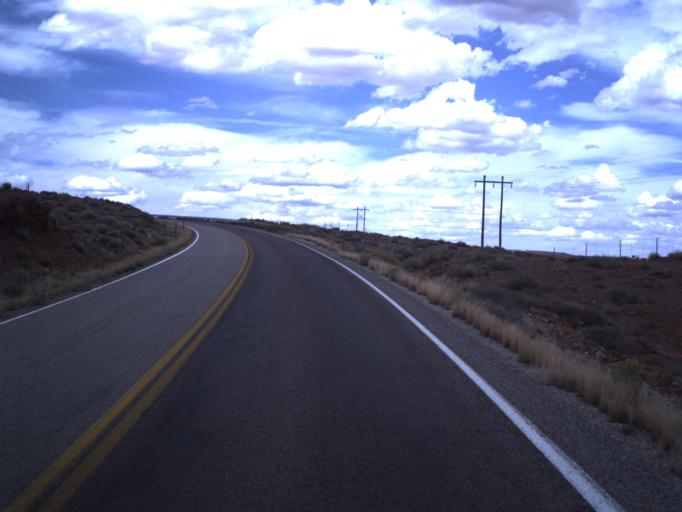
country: US
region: Utah
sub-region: San Juan County
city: Blanding
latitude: 37.1802
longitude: -109.8594
